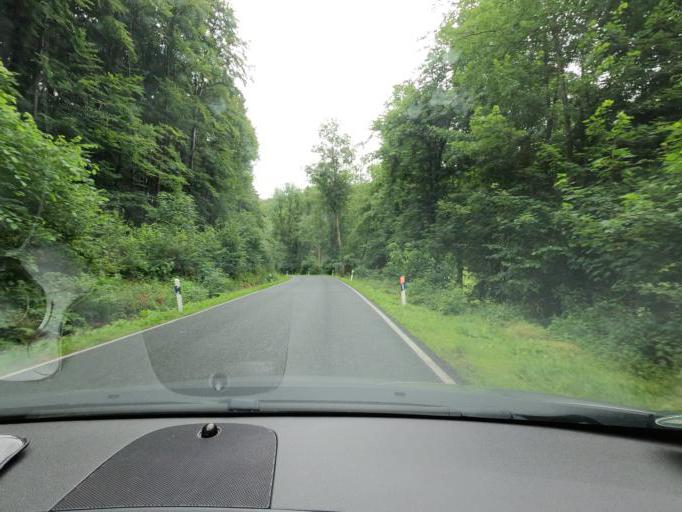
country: DE
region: Thuringia
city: Geisleden
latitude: 51.3326
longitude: 10.1635
